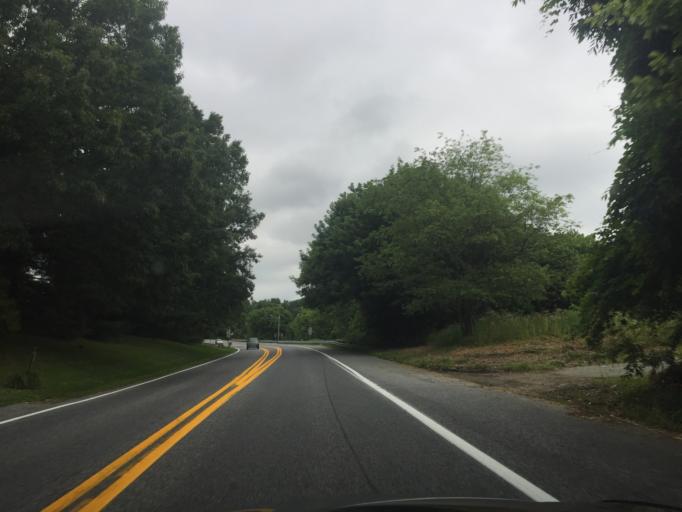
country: US
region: Maryland
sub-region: Harford County
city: Jarrettsville
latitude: 39.5884
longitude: -76.5094
